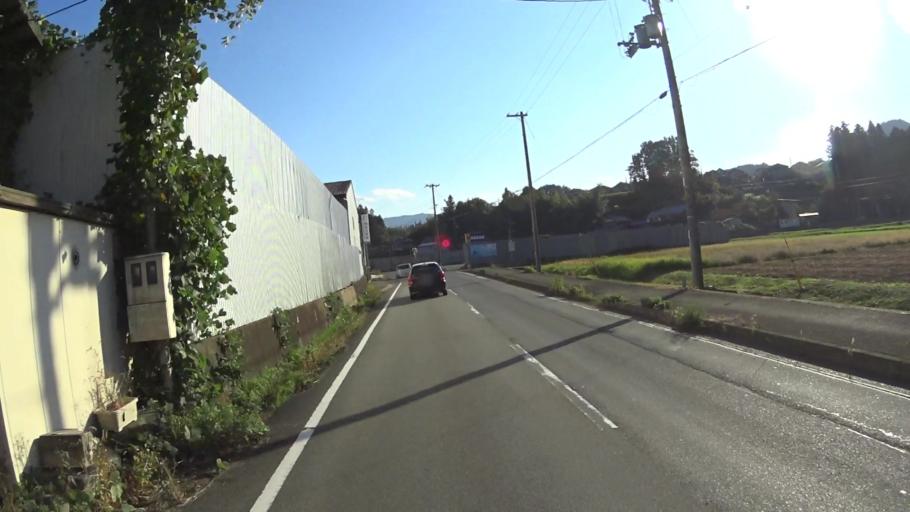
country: JP
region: Kyoto
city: Fukuchiyama
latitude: 35.3236
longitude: 135.1066
